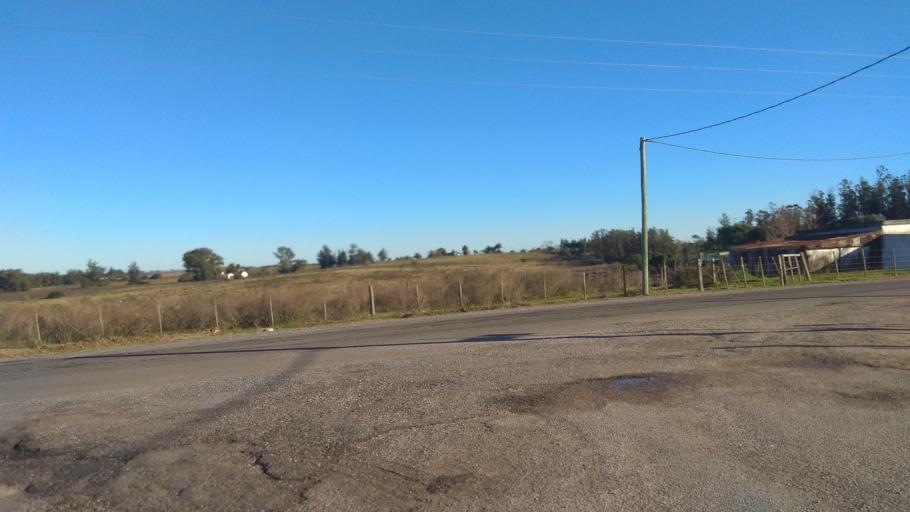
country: UY
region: Florida
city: Florida
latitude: -34.0970
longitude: -56.2405
